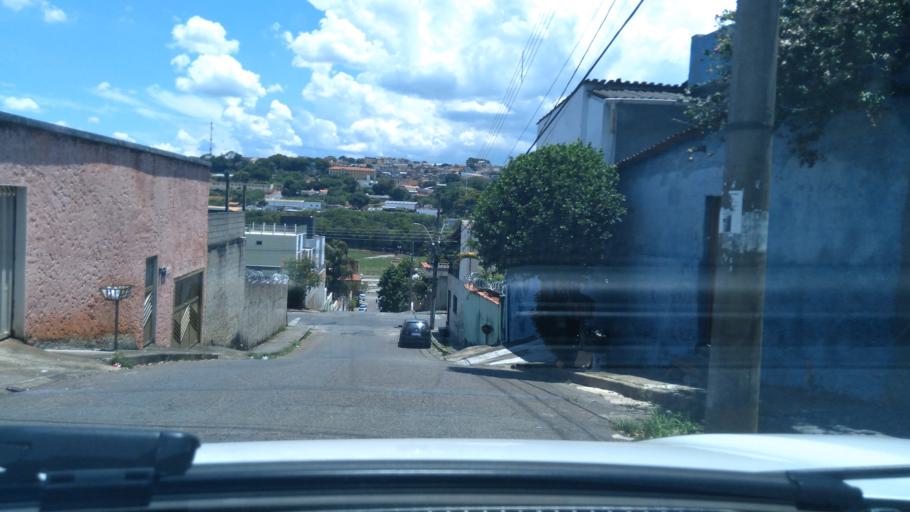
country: BR
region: Minas Gerais
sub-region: Contagem
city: Contagem
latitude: -19.9339
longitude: -43.9989
